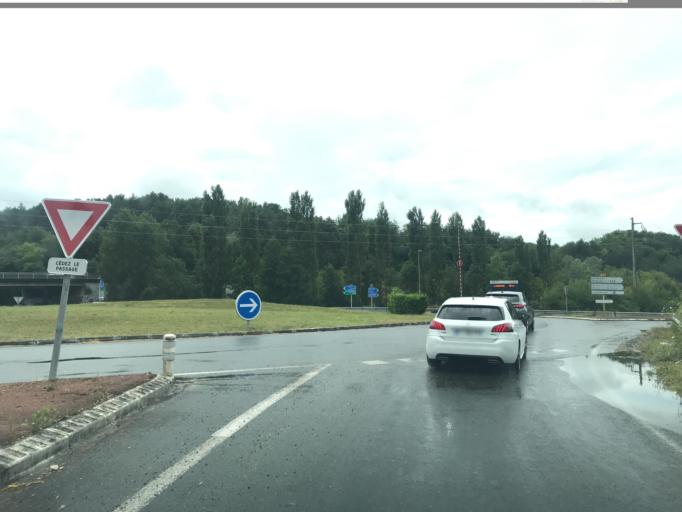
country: FR
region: Aquitaine
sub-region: Departement de la Dordogne
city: Coulounieix-Chamiers
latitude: 45.1423
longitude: 0.7000
